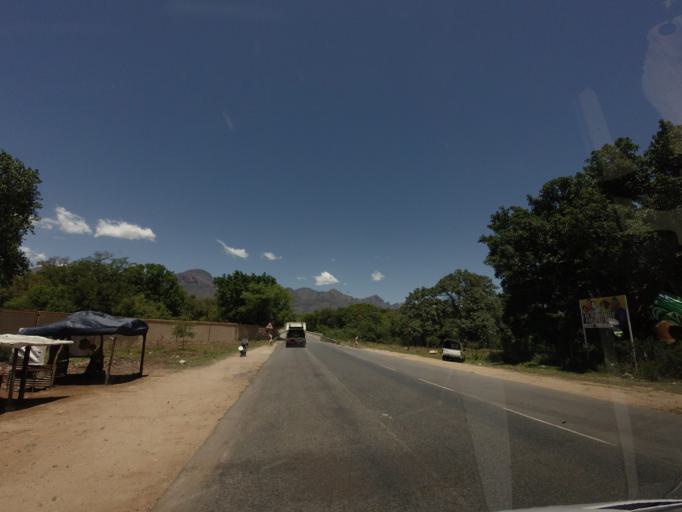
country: ZA
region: Limpopo
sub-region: Mopani District Municipality
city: Hoedspruit
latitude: -24.4045
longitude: 30.7991
